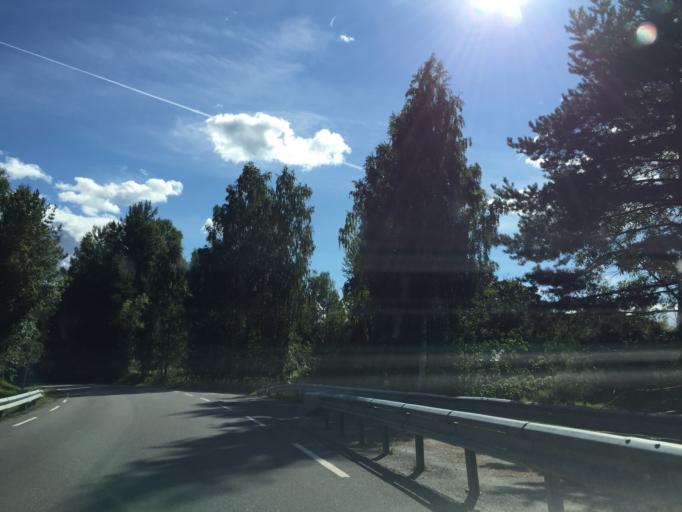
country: NO
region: Buskerud
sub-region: Ovre Eiker
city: Hokksund
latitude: 59.6996
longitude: 9.8440
